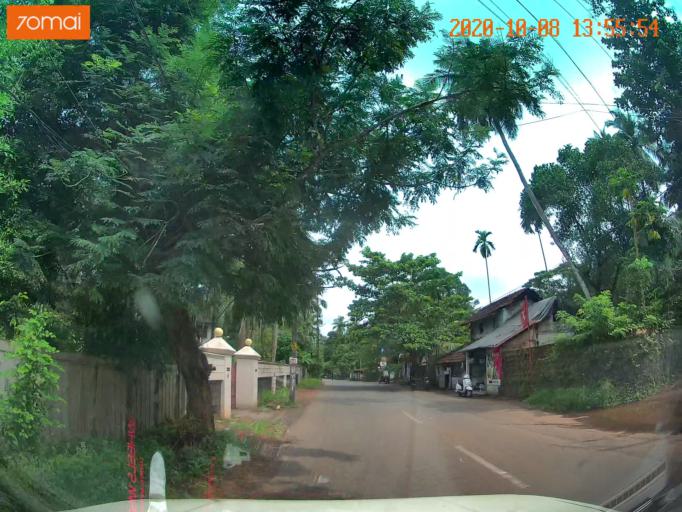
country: IN
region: Kerala
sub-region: Kozhikode
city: Kozhikode
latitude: 11.2928
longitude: 75.7966
